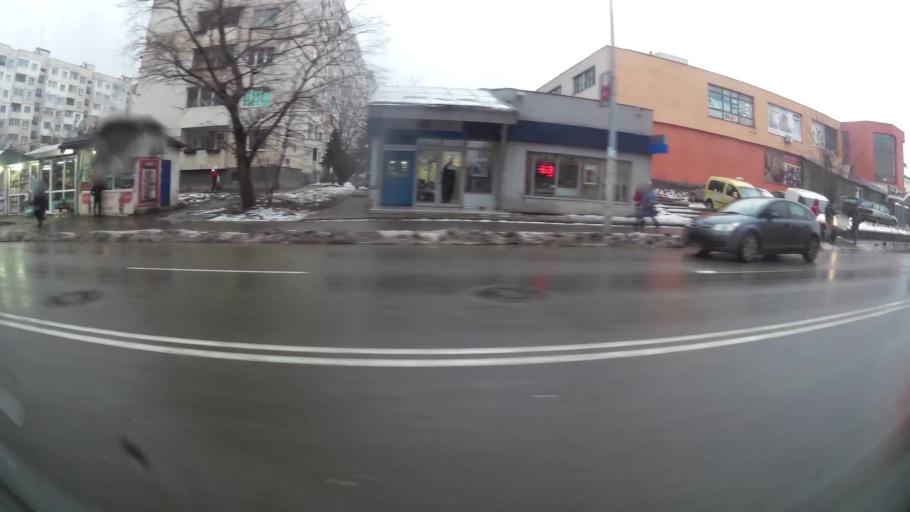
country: BG
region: Sofia-Capital
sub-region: Stolichna Obshtina
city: Sofia
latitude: 42.6899
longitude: 23.2548
